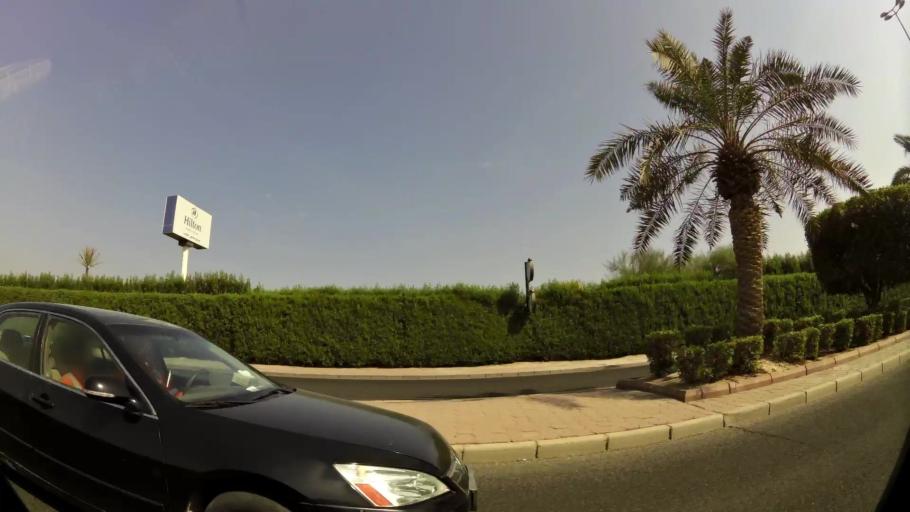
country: KW
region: Al Ahmadi
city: Al Manqaf
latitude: 29.1138
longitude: 48.1354
